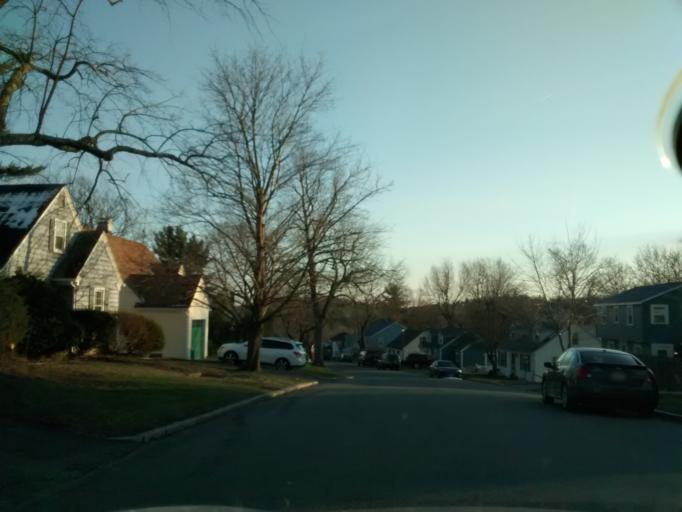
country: US
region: Massachusetts
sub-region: Worcester County
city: Worcester
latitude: 42.2919
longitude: -71.8100
